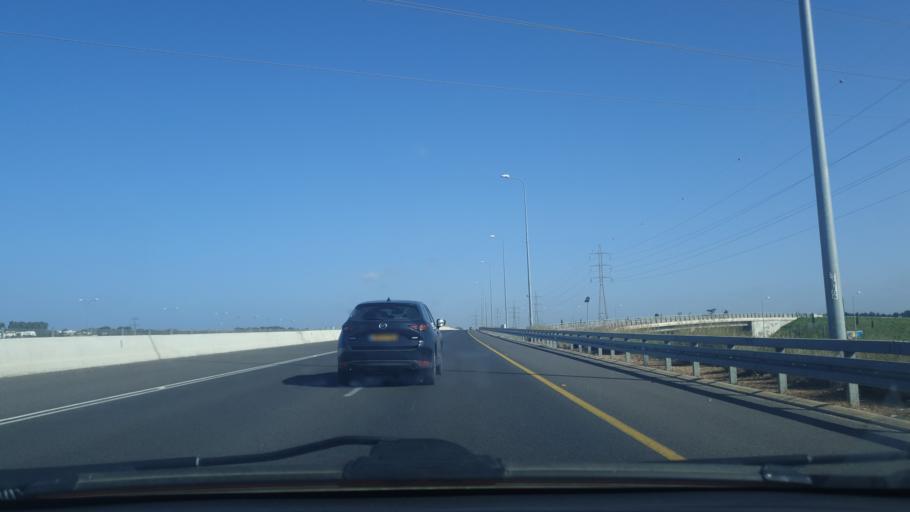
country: IL
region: Tel Aviv
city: Kefar Shemaryahu
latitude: 32.1957
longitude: 34.8310
